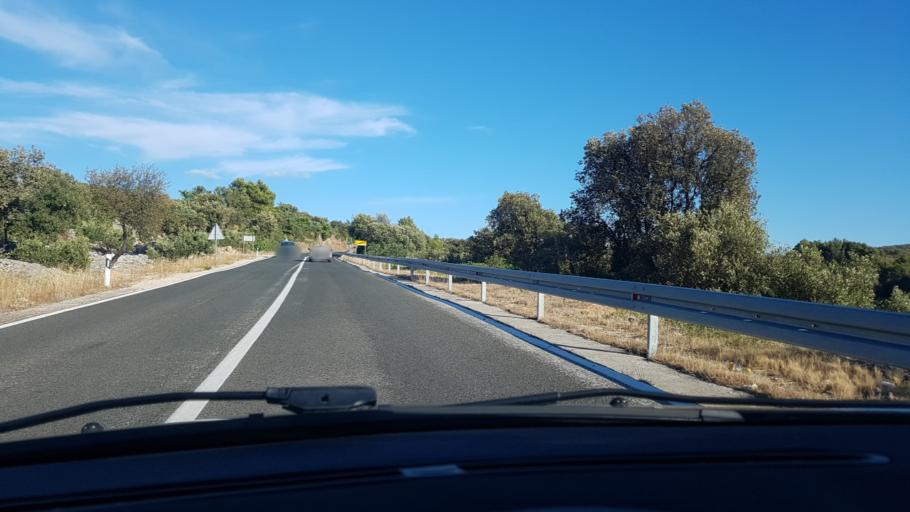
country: HR
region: Sibensko-Kniniska
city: Primosten
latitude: 43.5815
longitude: 15.9353
